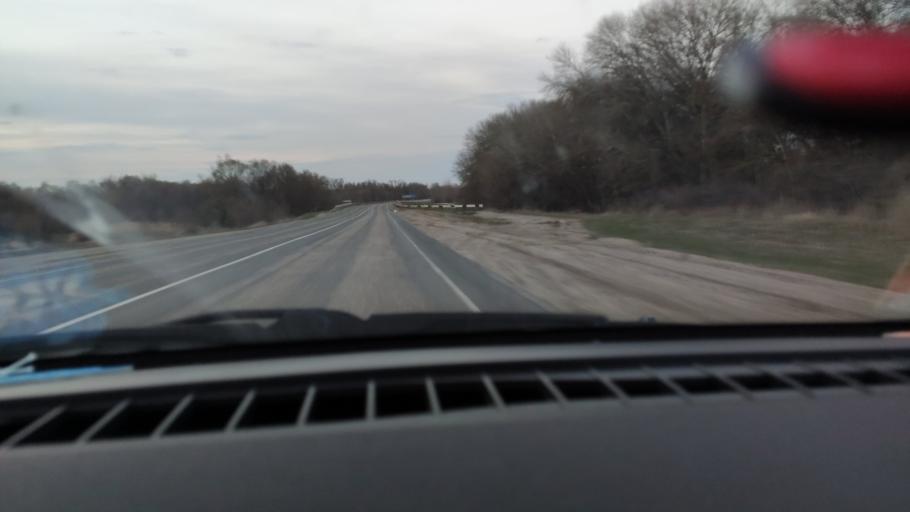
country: RU
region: Saratov
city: Sinodskoye
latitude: 51.9786
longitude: 46.6522
